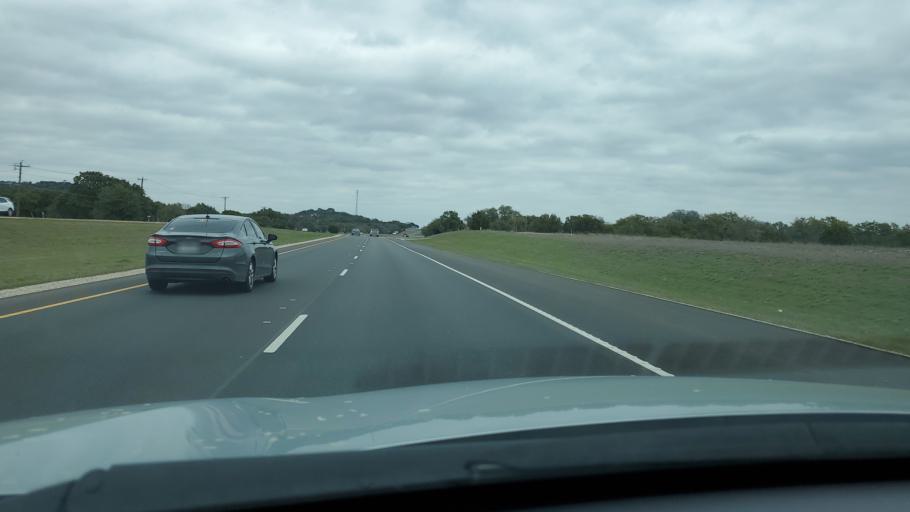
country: US
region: Texas
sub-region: Bell County
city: Killeen
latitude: 30.9942
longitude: -97.7624
